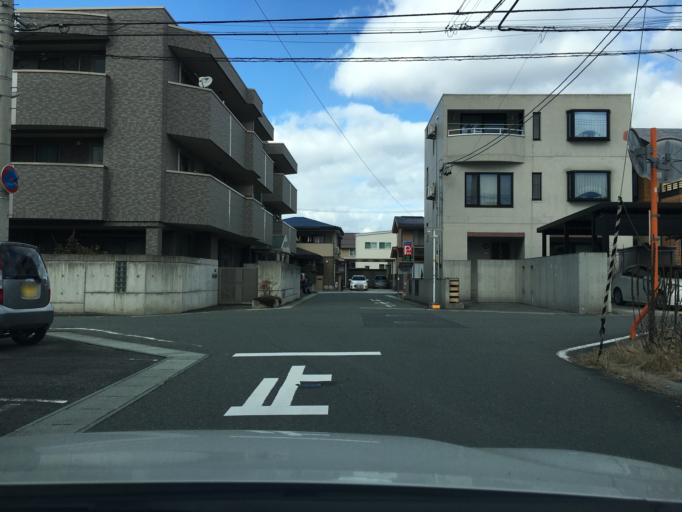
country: JP
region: Yamagata
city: Yamagata-shi
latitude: 38.2529
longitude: 140.3242
